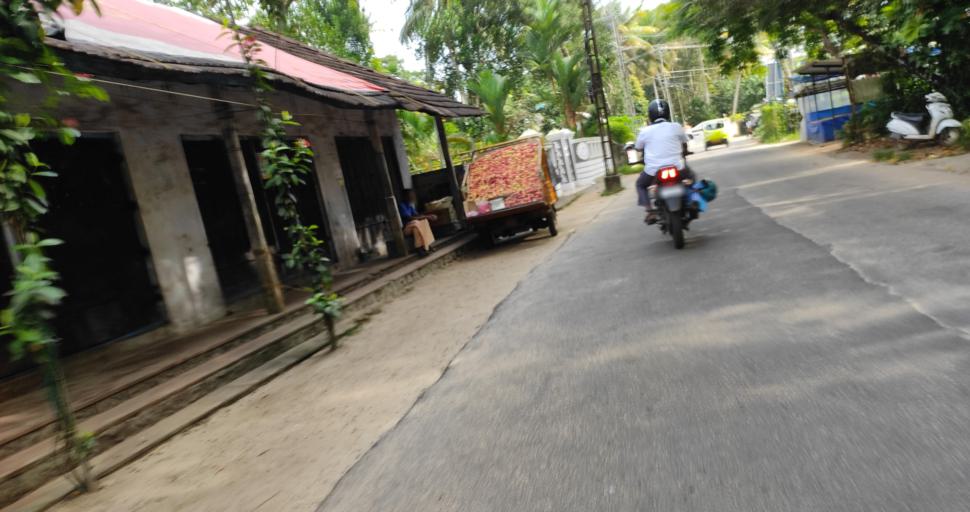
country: IN
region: Kerala
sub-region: Alappuzha
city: Vayalar
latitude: 9.6636
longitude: 76.2994
